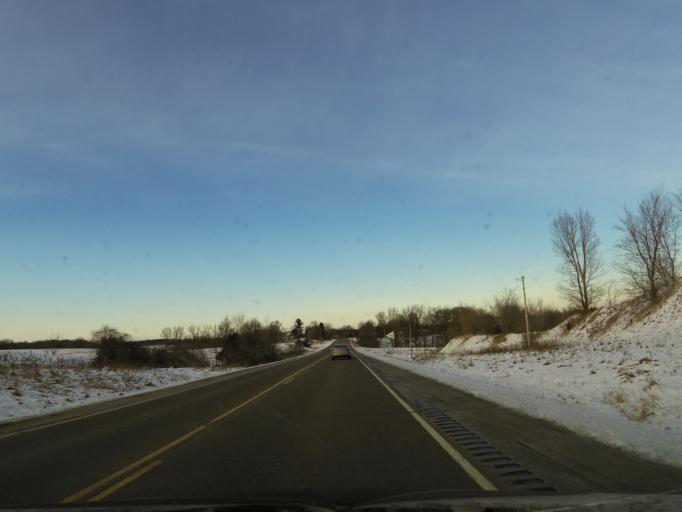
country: US
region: Wisconsin
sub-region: Polk County
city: Osceola
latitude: 45.3532
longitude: -92.7127
